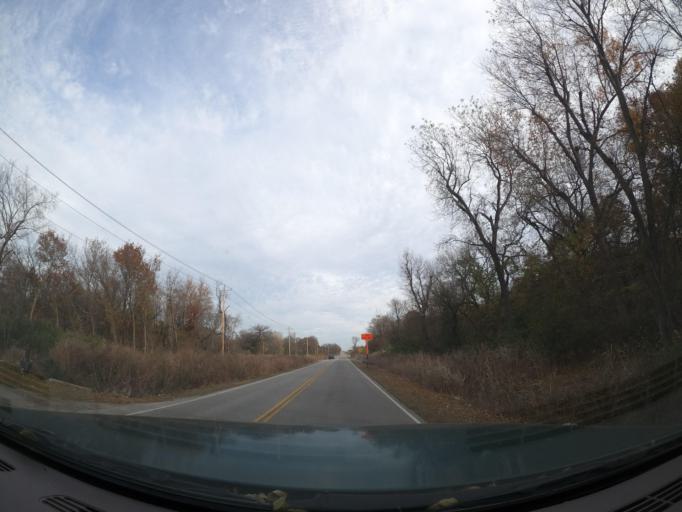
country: US
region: Oklahoma
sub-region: Tulsa County
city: Turley
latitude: 36.2060
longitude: -95.9717
